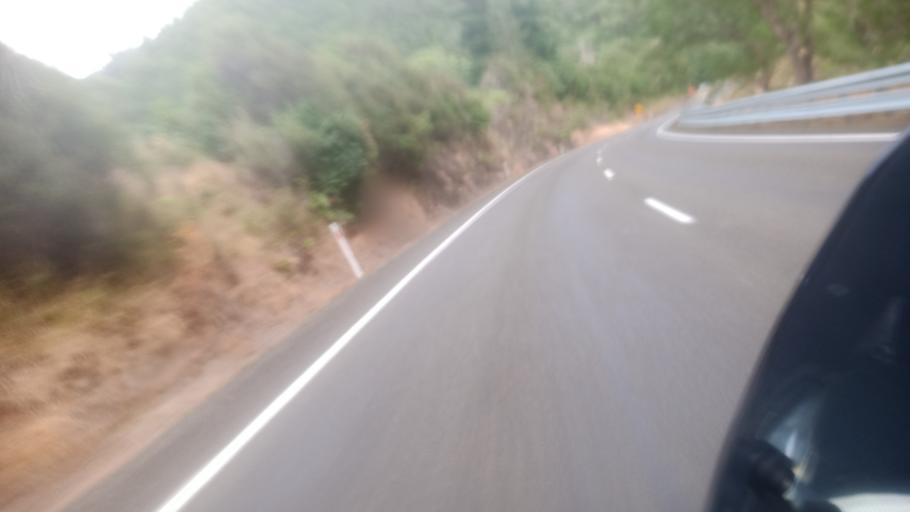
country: NZ
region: Bay of Plenty
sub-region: Opotiki District
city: Opotiki
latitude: -38.3427
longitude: 177.4437
